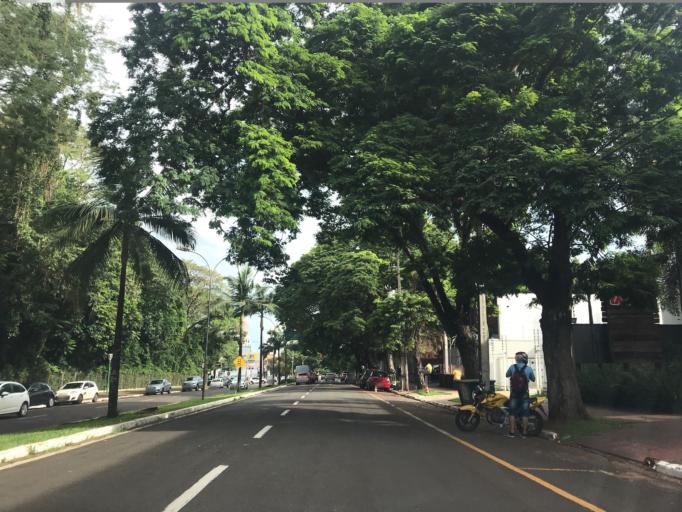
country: BR
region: Parana
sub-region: Maringa
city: Maringa
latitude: -23.4323
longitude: -51.9296
